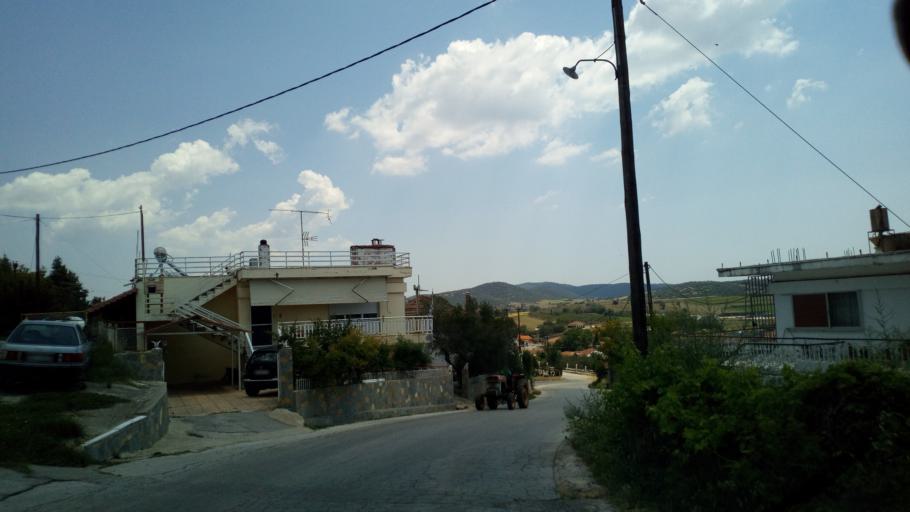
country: GR
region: Central Macedonia
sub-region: Nomos Thessalonikis
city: Askos
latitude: 40.7531
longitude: 23.3849
